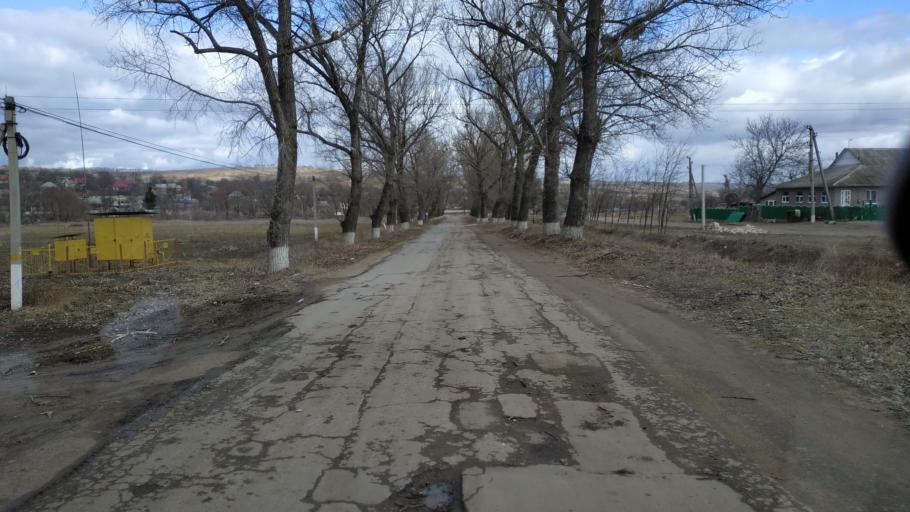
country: MD
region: Calarasi
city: Calarasi
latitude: 47.1288
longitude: 28.3108
